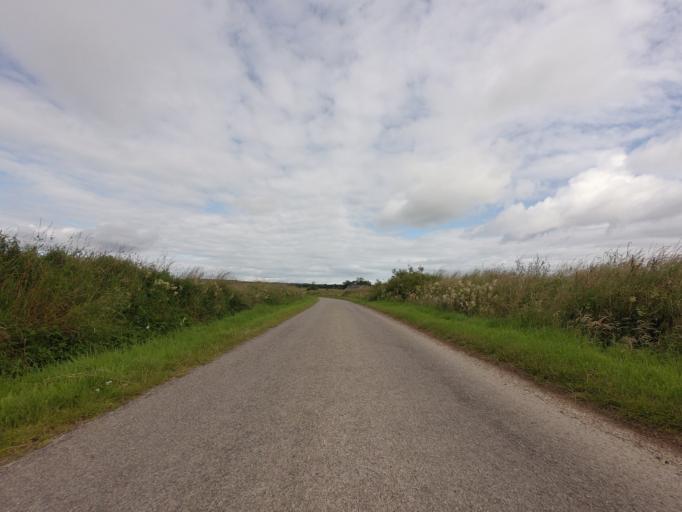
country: GB
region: Scotland
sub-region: Moray
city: Elgin
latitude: 57.6690
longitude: -3.3808
